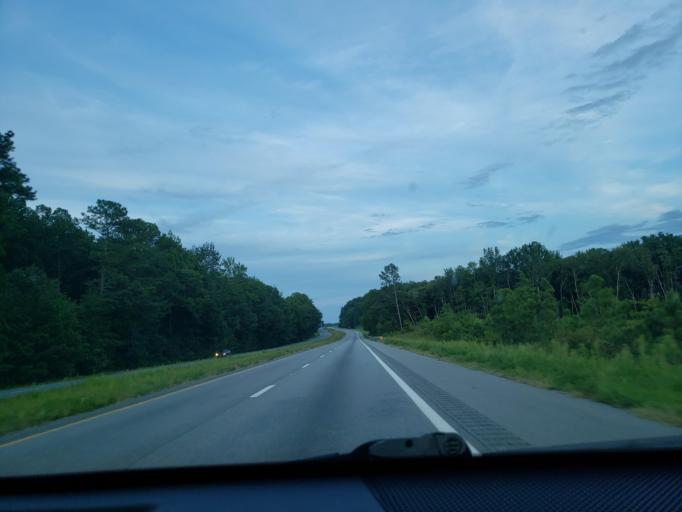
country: US
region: Virginia
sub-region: Southampton County
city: Courtland
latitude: 36.7040
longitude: -77.2766
